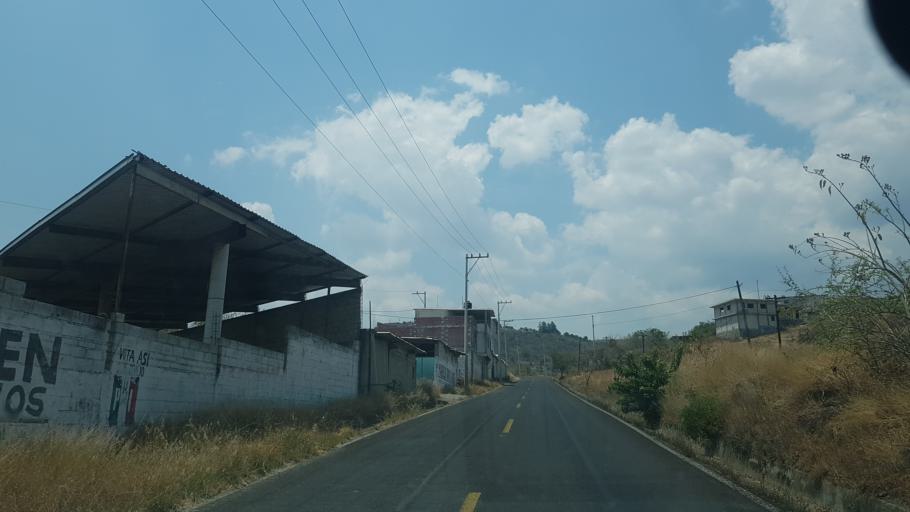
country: MX
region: Puebla
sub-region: Atzitzihuacan
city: Santiago Atzitzihuacan
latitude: 18.8335
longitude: -98.5922
